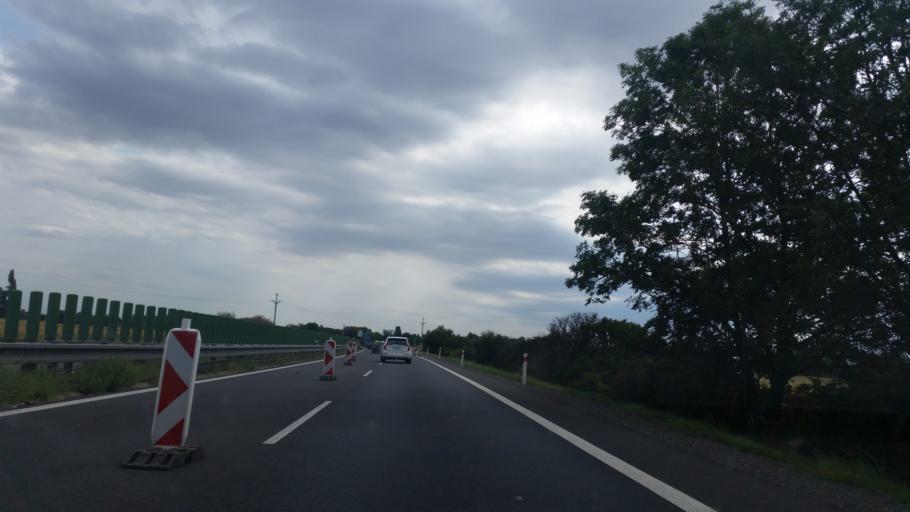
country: CZ
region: Olomoucky
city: Hnevotin
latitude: 49.5412
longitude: 17.1758
